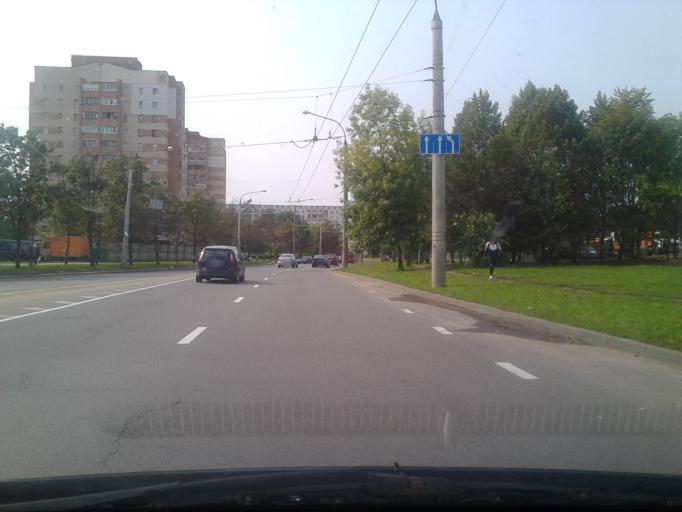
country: BY
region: Minsk
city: Novoye Medvezhino
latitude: 53.8714
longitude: 27.4737
